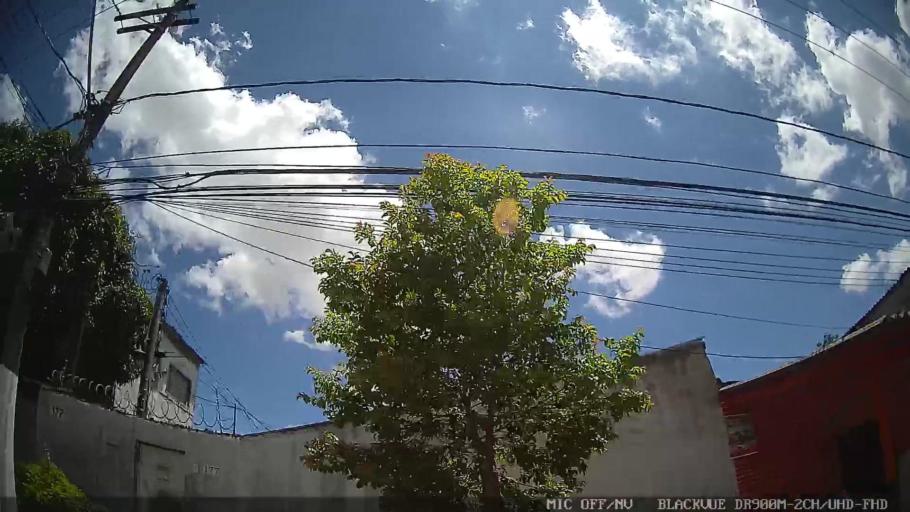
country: BR
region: Sao Paulo
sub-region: Diadema
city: Diadema
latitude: -23.6548
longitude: -46.6462
